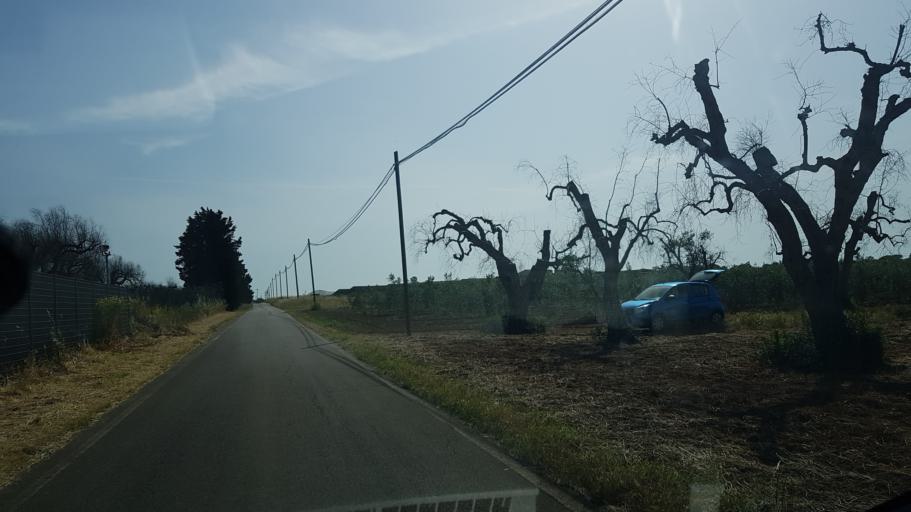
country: IT
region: Apulia
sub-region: Provincia di Brindisi
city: Torchiarolo
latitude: 40.5129
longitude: 18.0781
